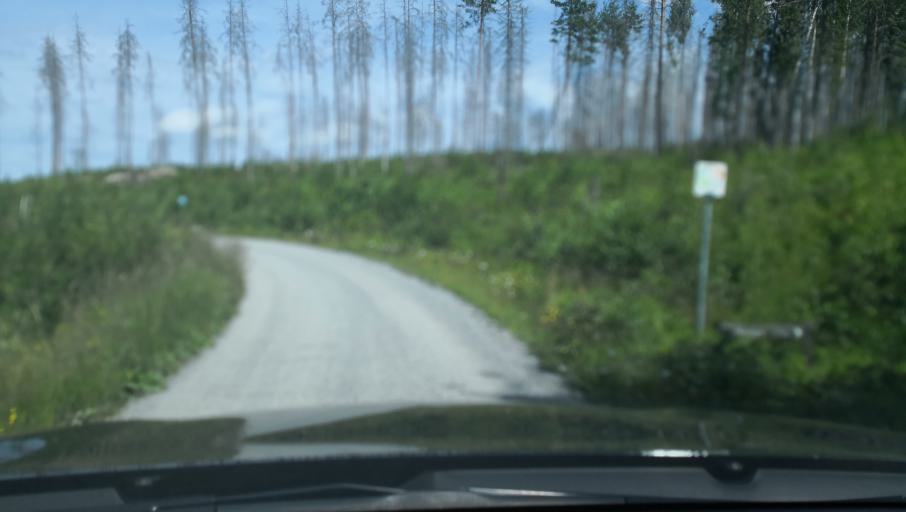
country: SE
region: Vaestmanland
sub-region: Surahammars Kommun
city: Ramnas
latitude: 59.8935
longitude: 16.1014
